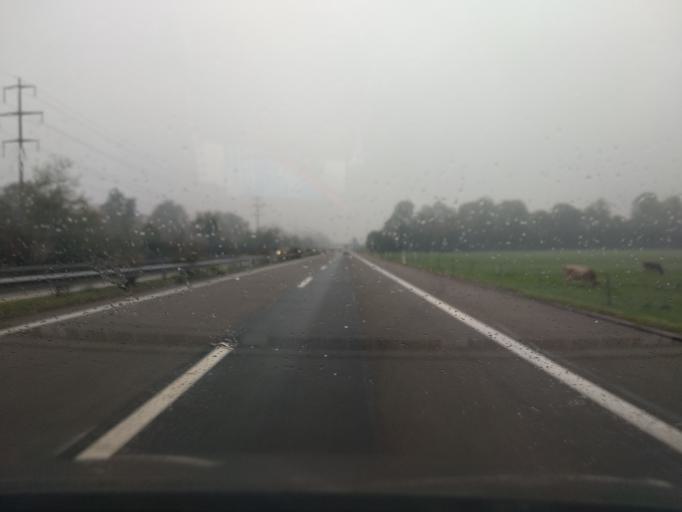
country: CH
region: Saint Gallen
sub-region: Wahlkreis Wil
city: Uzwil
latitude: 47.4553
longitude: 9.1296
